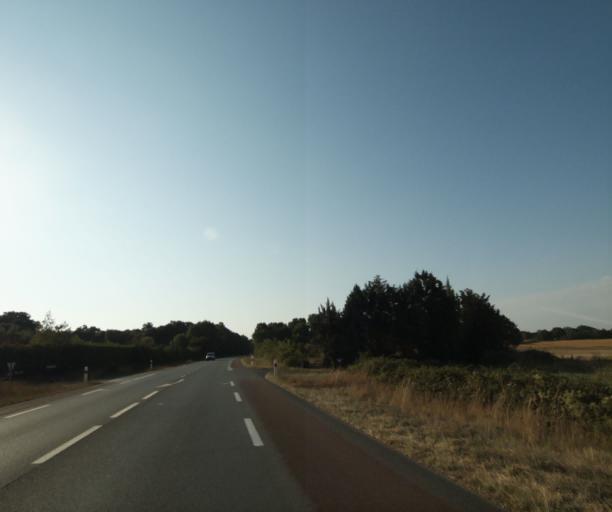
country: FR
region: Poitou-Charentes
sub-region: Departement de la Charente-Maritime
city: Cabariot
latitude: 45.9488
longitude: -0.8676
